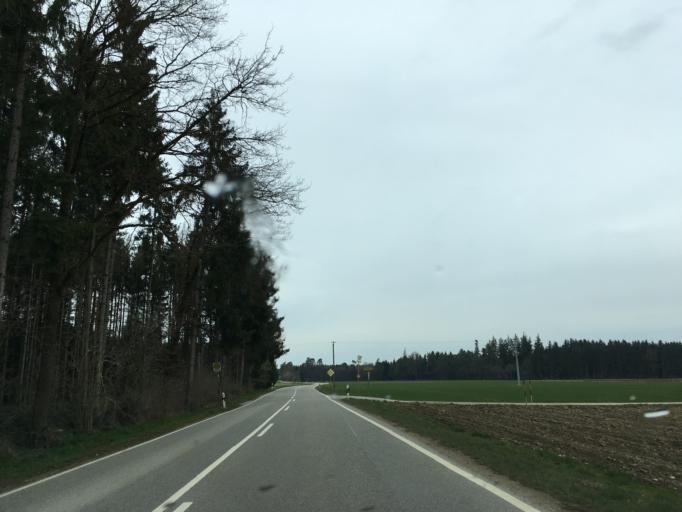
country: DE
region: Bavaria
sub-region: Upper Bavaria
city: Schnaitsee
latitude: 48.0850
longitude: 12.4096
